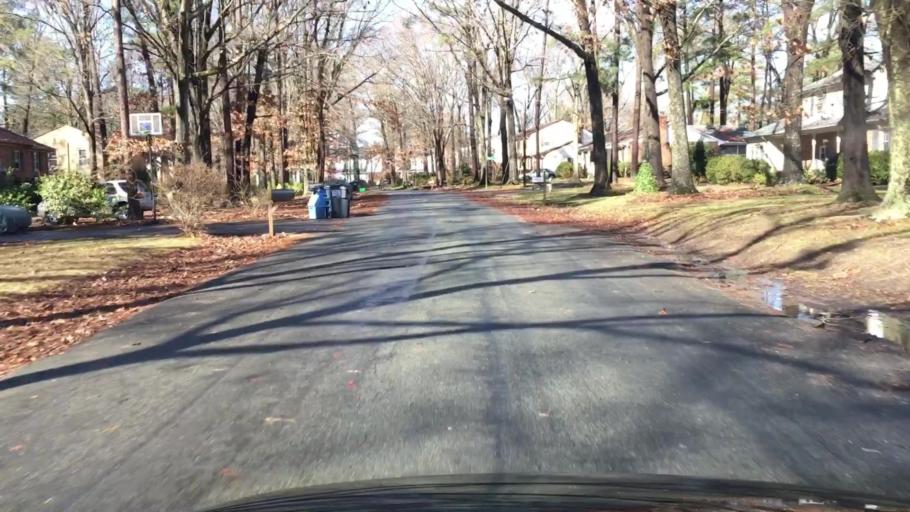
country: US
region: Virginia
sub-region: Chesterfield County
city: Bon Air
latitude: 37.5272
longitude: -77.5938
